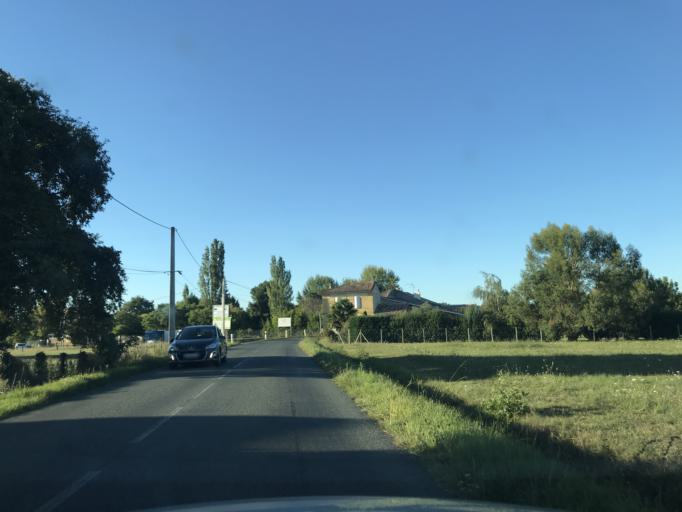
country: FR
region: Aquitaine
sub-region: Departement de la Gironde
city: Mouliets-et-Villemartin
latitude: 44.8356
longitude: -0.0388
